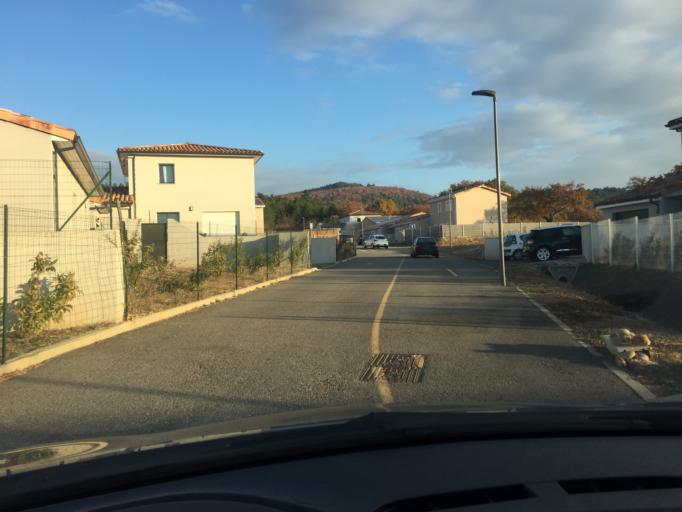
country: FR
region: Rhone-Alpes
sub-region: Departement de la Drome
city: Donzere
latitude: 44.4546
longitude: 4.7214
